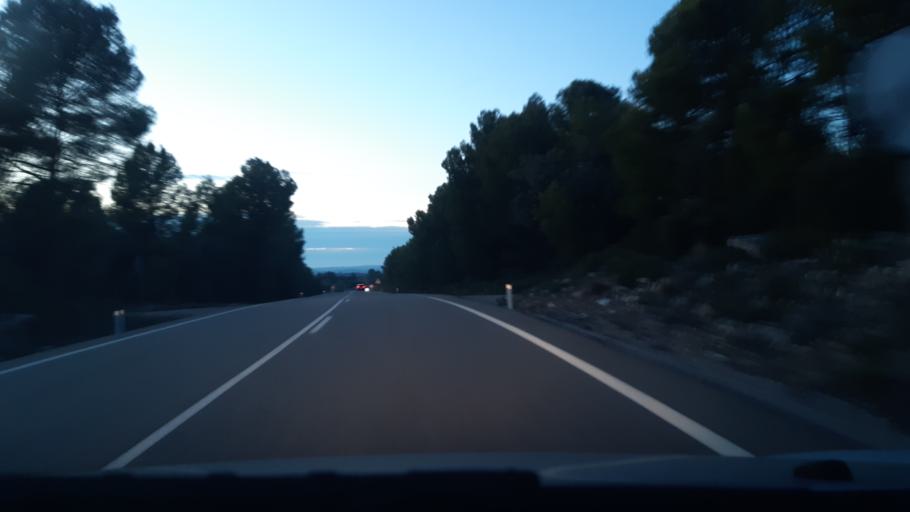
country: ES
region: Aragon
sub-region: Provincia de Teruel
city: Calaceite
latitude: 40.9620
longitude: 0.2120
